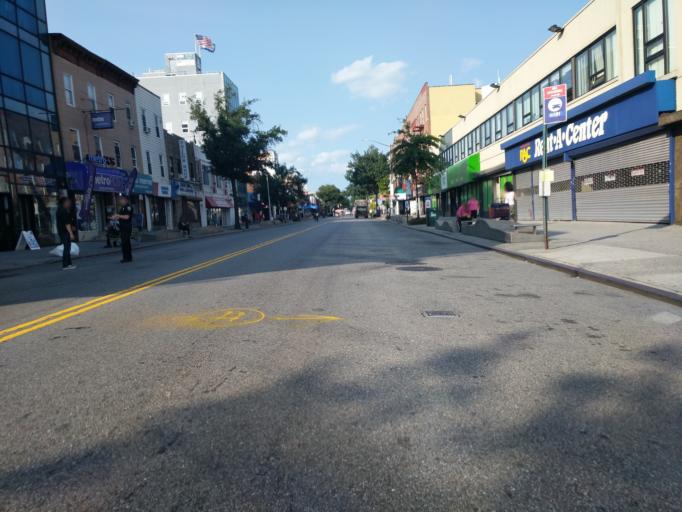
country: US
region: New York
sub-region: Queens County
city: Long Island City
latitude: 40.7570
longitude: -73.9205
